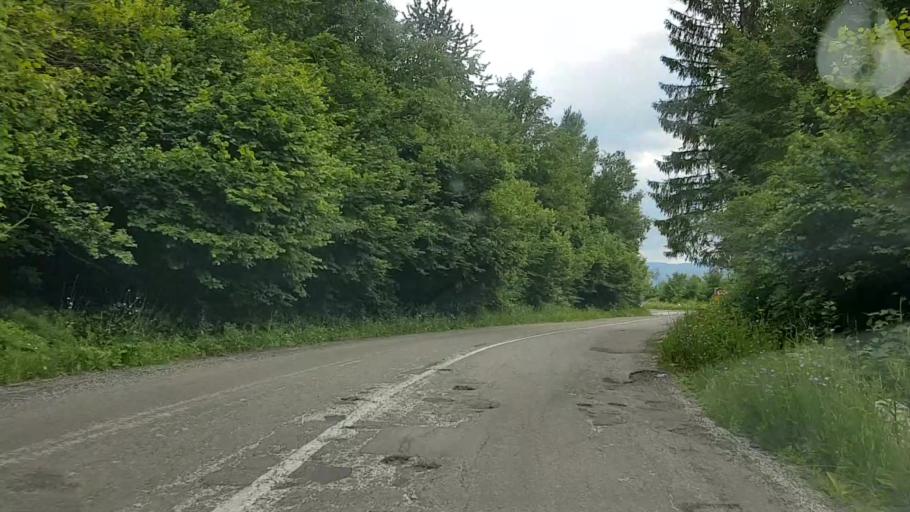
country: RO
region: Neamt
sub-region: Comuna Pangarati
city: Pangarati
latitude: 46.9595
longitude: 26.1228
